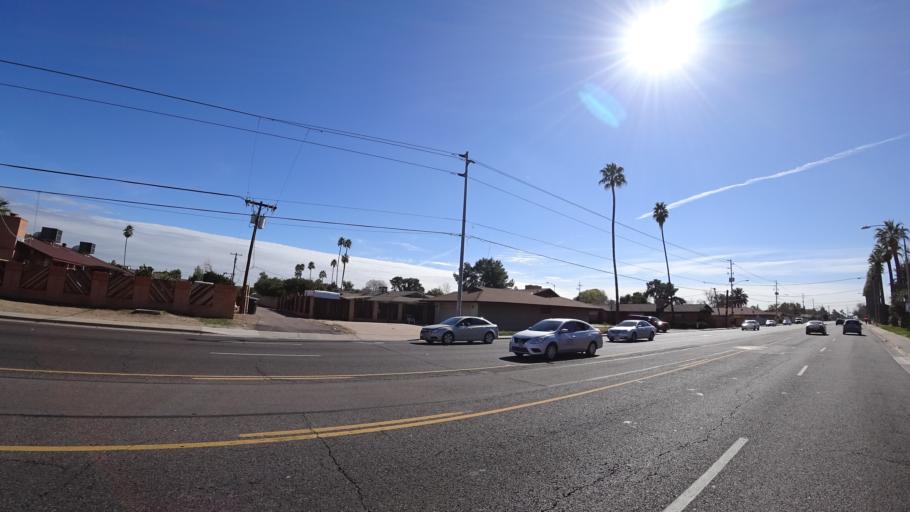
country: US
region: Arizona
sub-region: Maricopa County
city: Glendale
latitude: 33.5490
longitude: -112.1863
